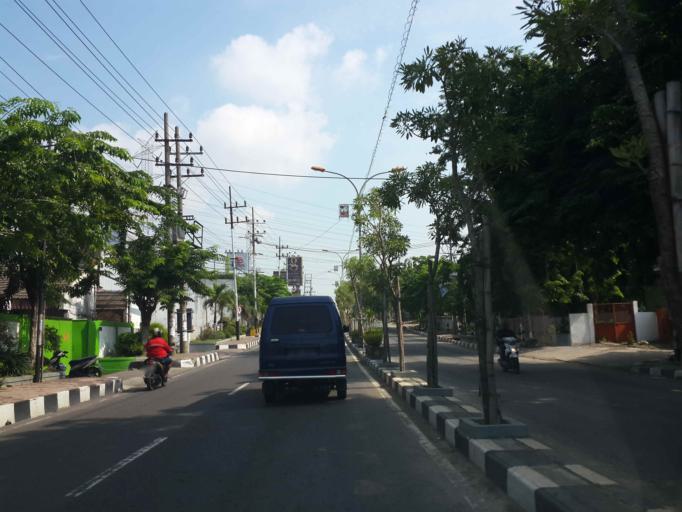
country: ID
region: East Java
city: Kebomas
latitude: -7.1870
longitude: 112.6475
